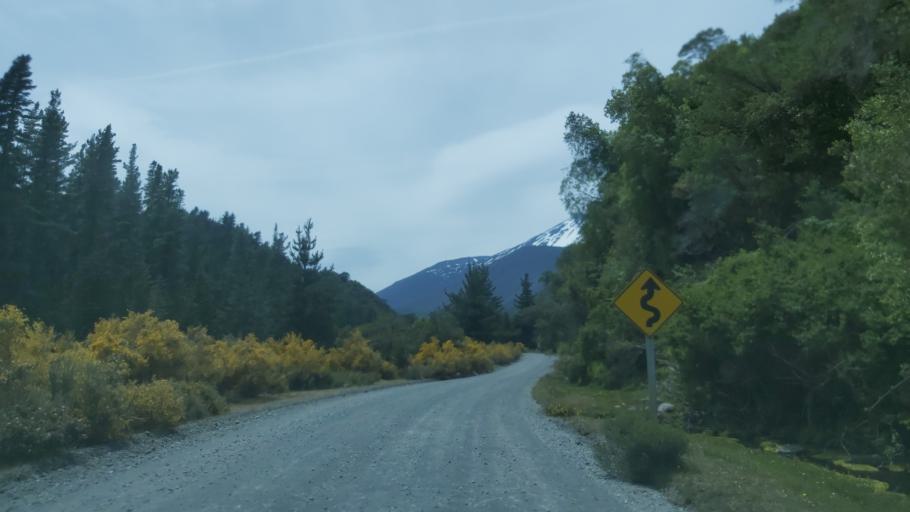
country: AR
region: Neuquen
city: Las Ovejas
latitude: -37.3968
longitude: -71.4526
